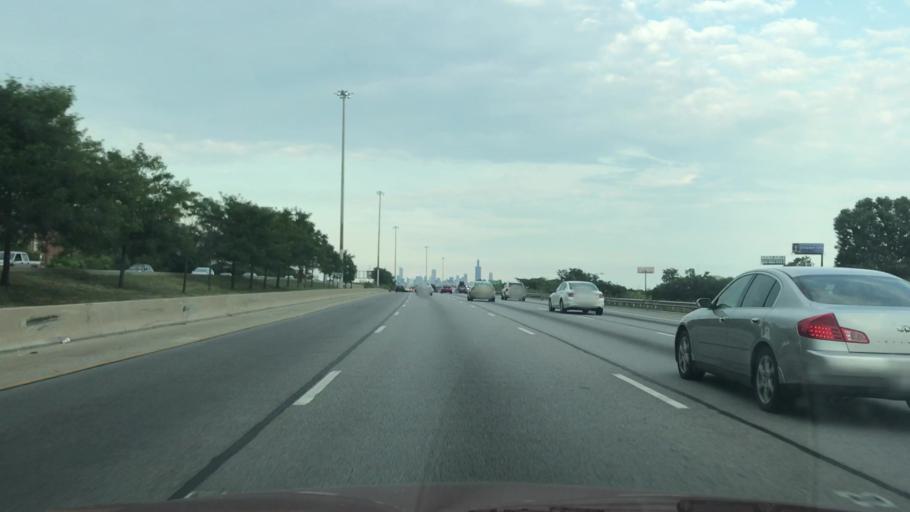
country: US
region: Illinois
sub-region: Cook County
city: Oak Park
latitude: 41.8707
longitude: -87.7669
